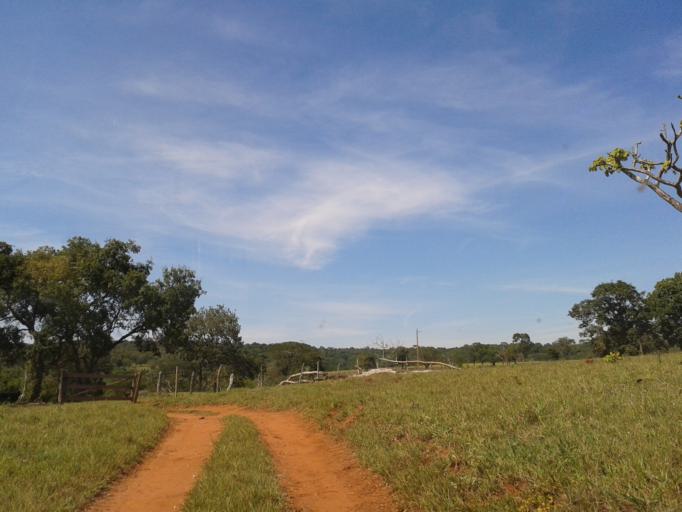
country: BR
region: Minas Gerais
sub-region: Campina Verde
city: Campina Verde
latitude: -19.4355
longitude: -49.6863
